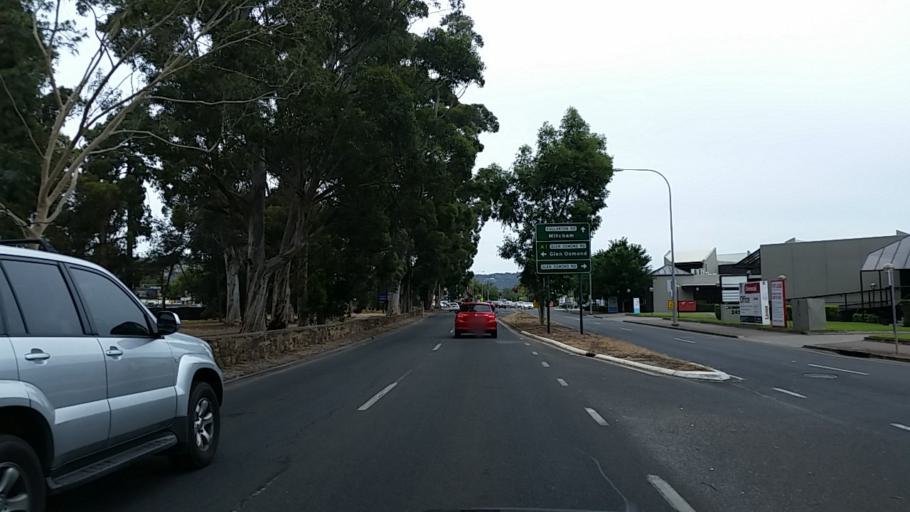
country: AU
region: South Australia
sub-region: Unley
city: Fullarton
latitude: -34.9447
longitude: 138.6250
